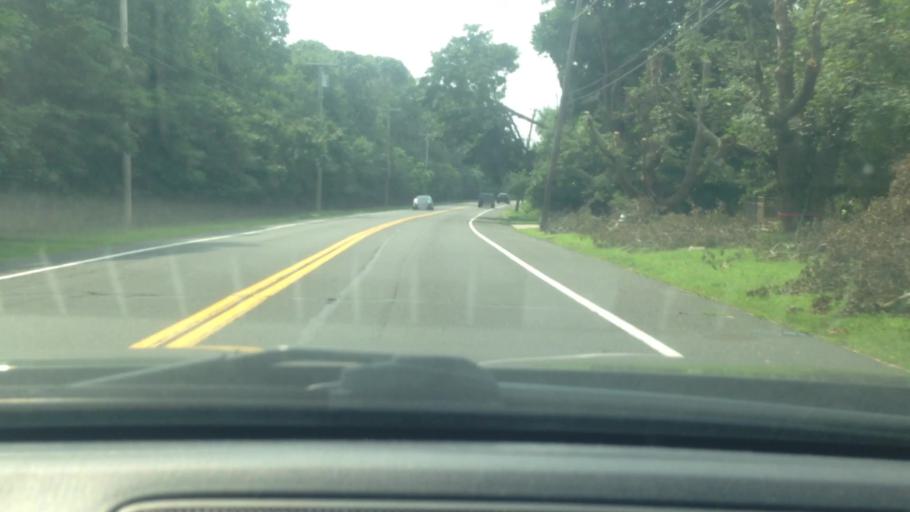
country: US
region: New York
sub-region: Suffolk County
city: Sag Harbor
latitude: 40.9685
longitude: -72.3001
